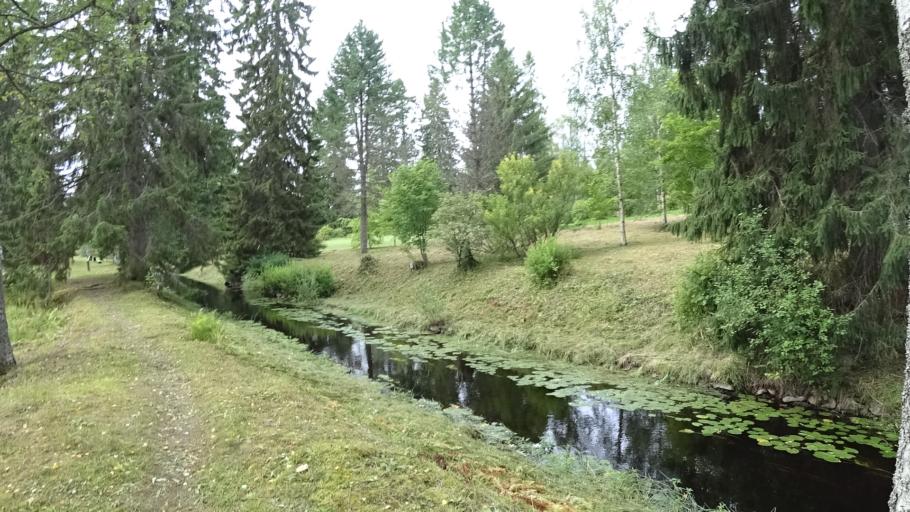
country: FI
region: North Karelia
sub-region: Joensuu
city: Ilomantsi
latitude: 62.6413
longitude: 31.2917
